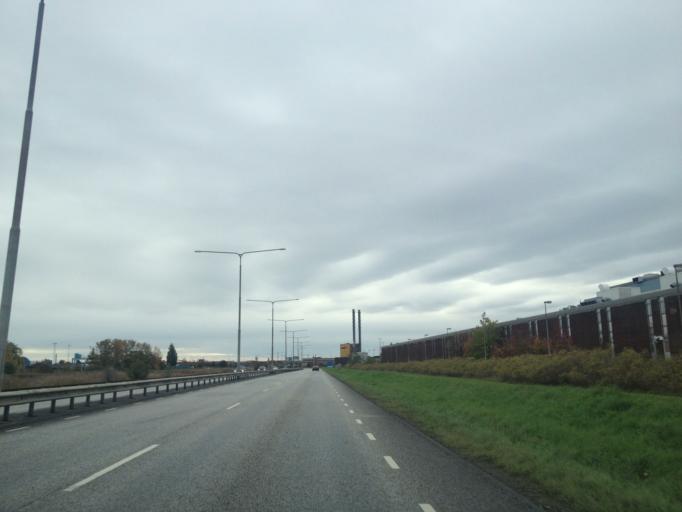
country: SE
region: Skane
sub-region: Burlovs Kommun
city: Arloev
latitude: 55.6243
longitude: 13.0491
